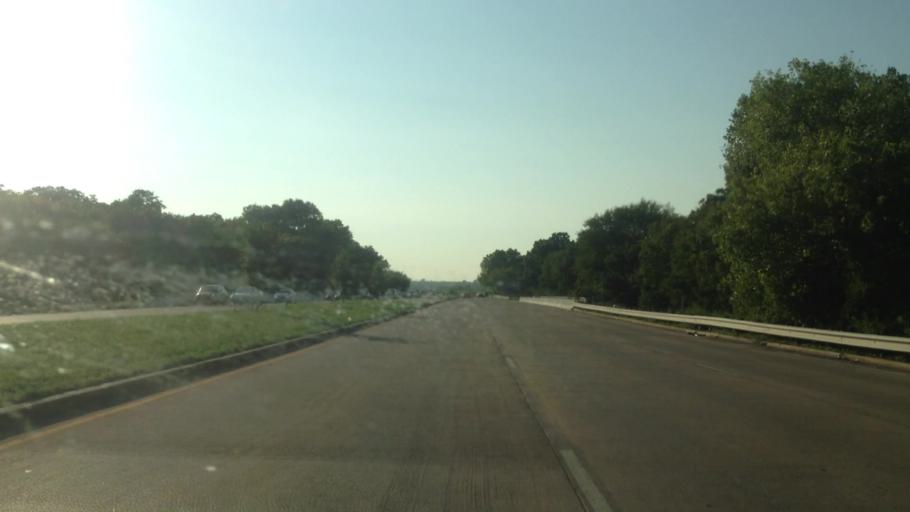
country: US
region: Texas
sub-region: Tarrant County
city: Pantego
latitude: 32.7176
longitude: -97.1719
